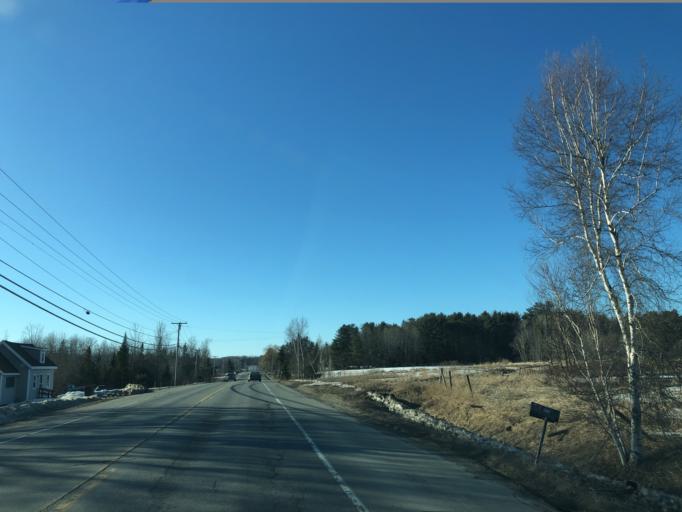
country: US
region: Maine
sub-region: Penobscot County
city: Levant
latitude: 44.8725
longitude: -68.8501
